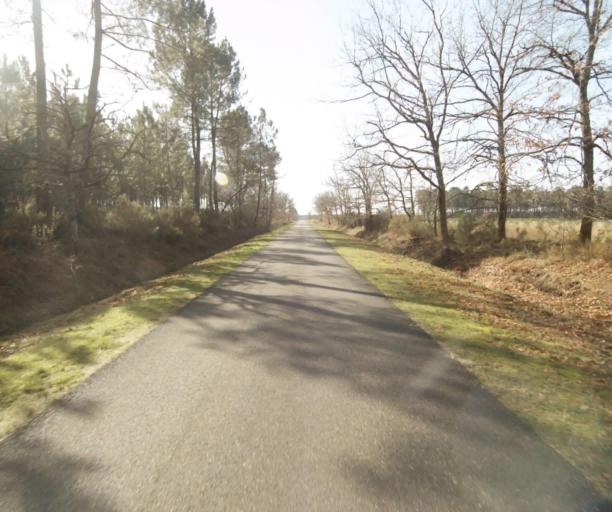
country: FR
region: Aquitaine
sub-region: Departement des Landes
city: Roquefort
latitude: 44.1843
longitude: -0.1552
